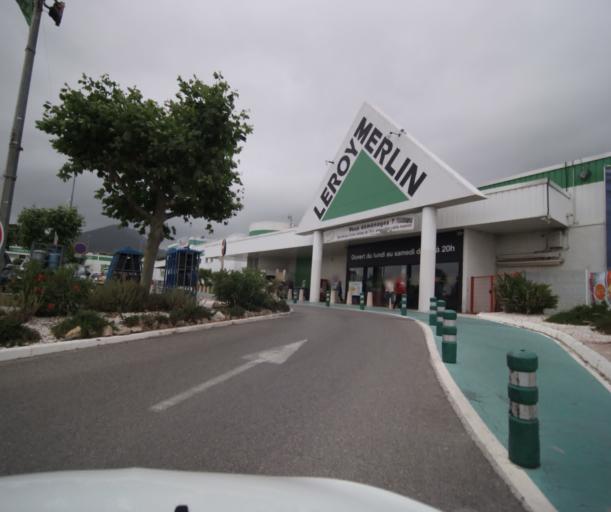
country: FR
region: Provence-Alpes-Cote d'Azur
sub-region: Departement du Var
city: La Garde
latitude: 43.1398
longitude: 6.0041
